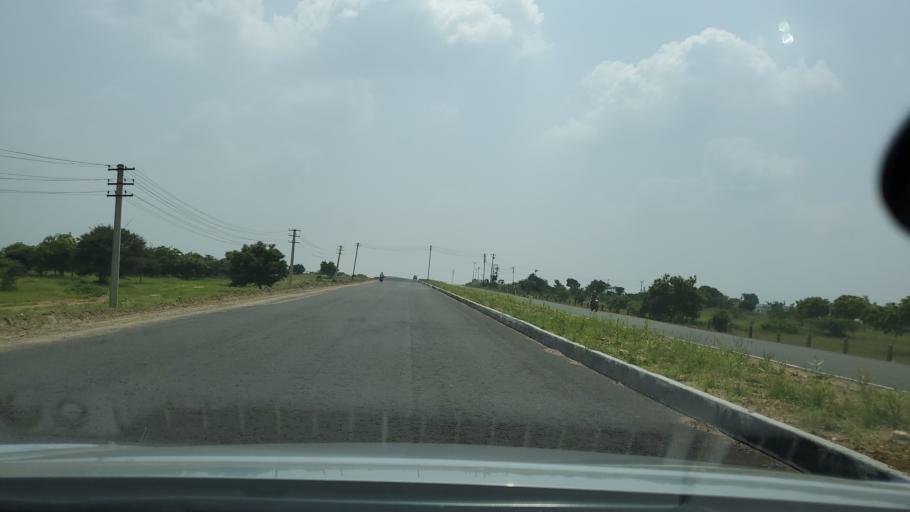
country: IN
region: Tamil Nadu
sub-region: Tiruppur
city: Dharapuram
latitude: 10.8694
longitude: 77.4632
